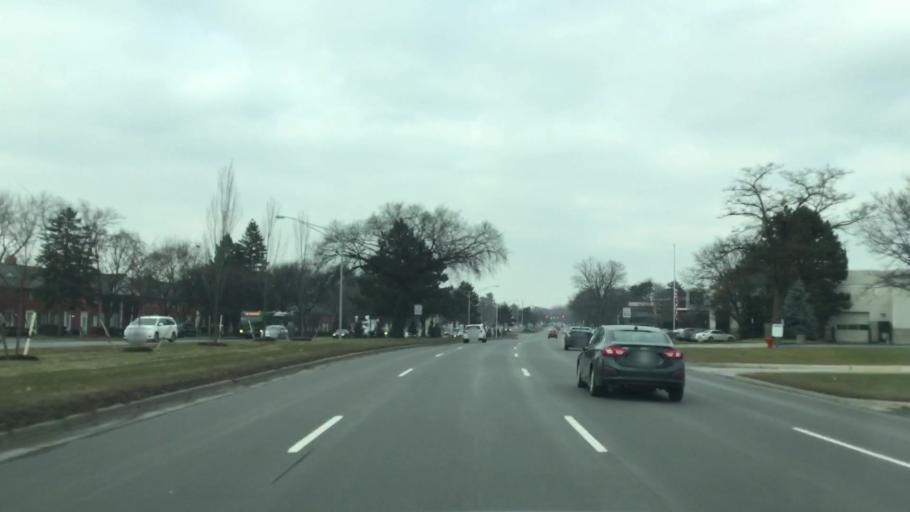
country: US
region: Michigan
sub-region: Oakland County
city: Birmingham
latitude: 42.5562
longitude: -83.2212
